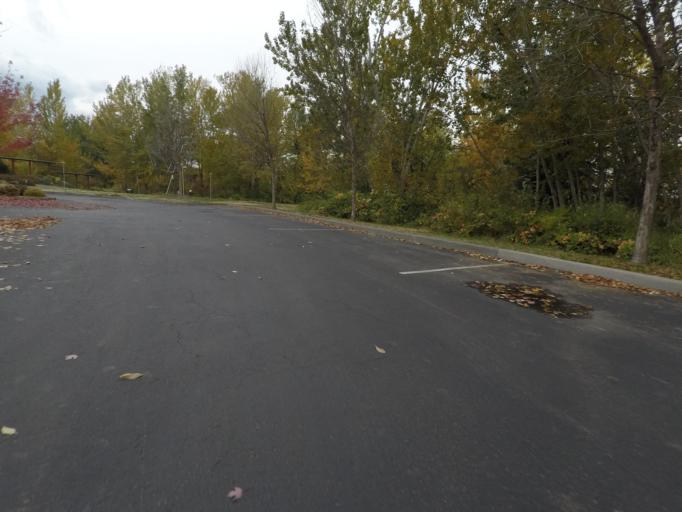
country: US
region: Washington
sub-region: Walla Walla County
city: Walla Walla East
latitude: 46.0785
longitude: -118.2744
